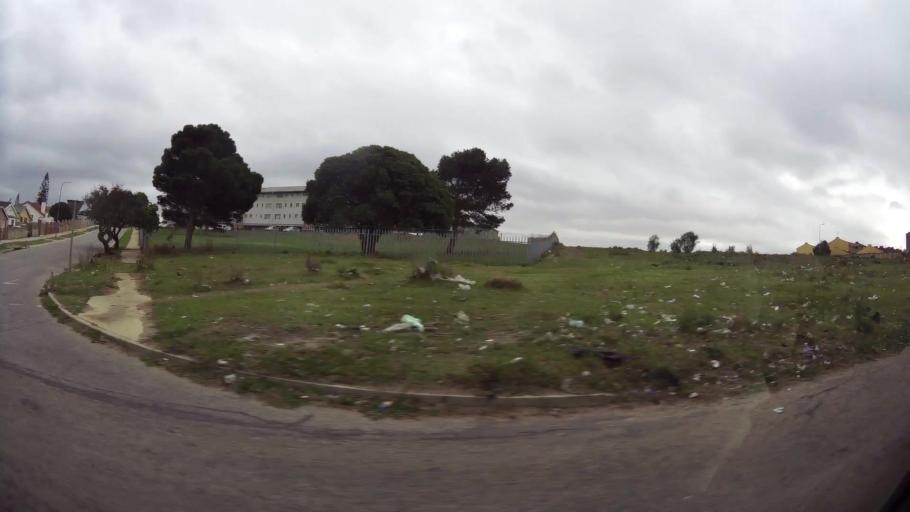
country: ZA
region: Eastern Cape
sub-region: Nelson Mandela Bay Metropolitan Municipality
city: Port Elizabeth
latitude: -33.9056
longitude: 25.5606
